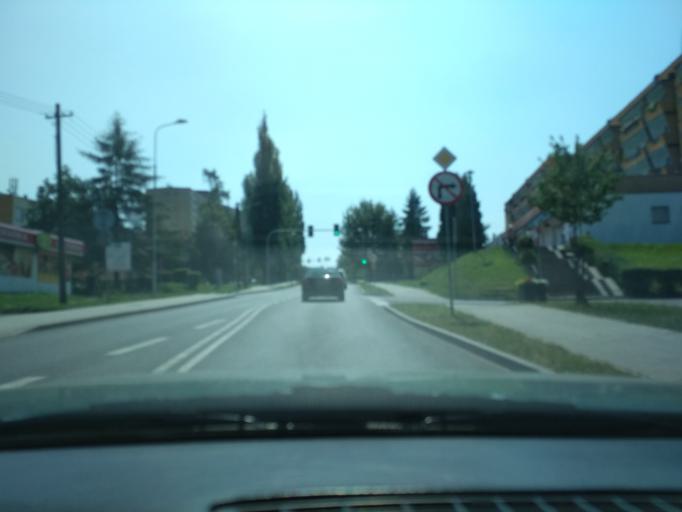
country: PL
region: Silesian Voivodeship
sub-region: Chorzow
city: Chorzow
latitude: 50.2996
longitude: 19.0030
